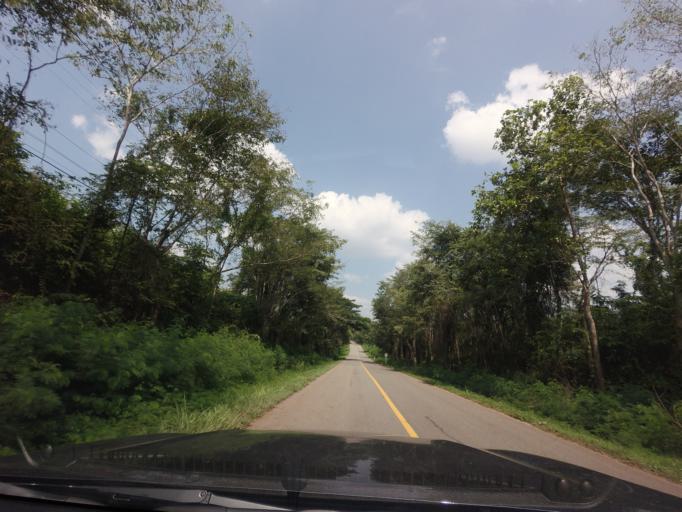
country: TH
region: Uttaradit
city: Ban Khok
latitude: 17.9201
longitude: 100.9955
